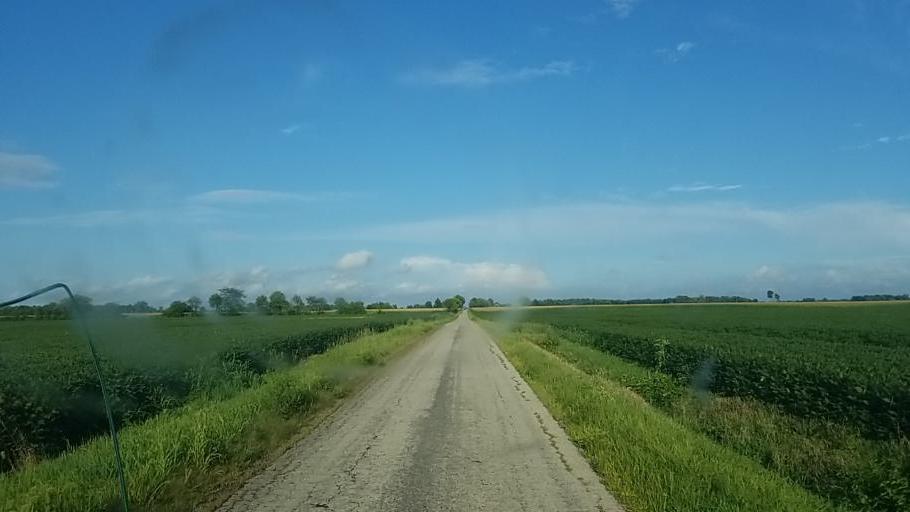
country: US
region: Ohio
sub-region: Crawford County
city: Bucyrus
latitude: 40.7394
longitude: -82.9770
